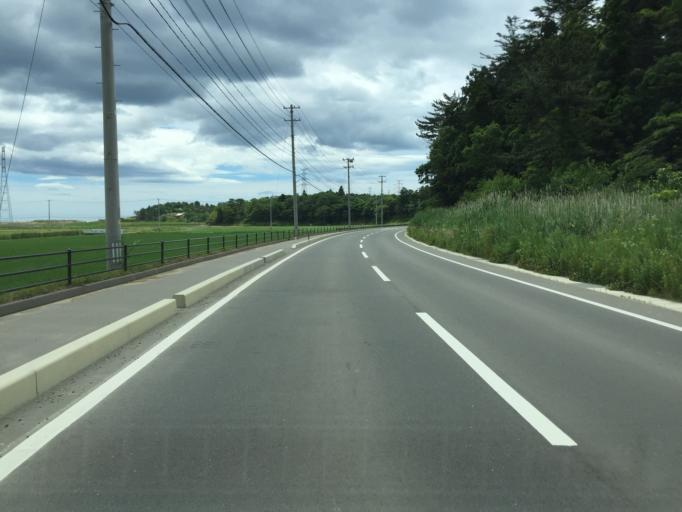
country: JP
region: Fukushima
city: Namie
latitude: 37.6626
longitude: 141.0061
